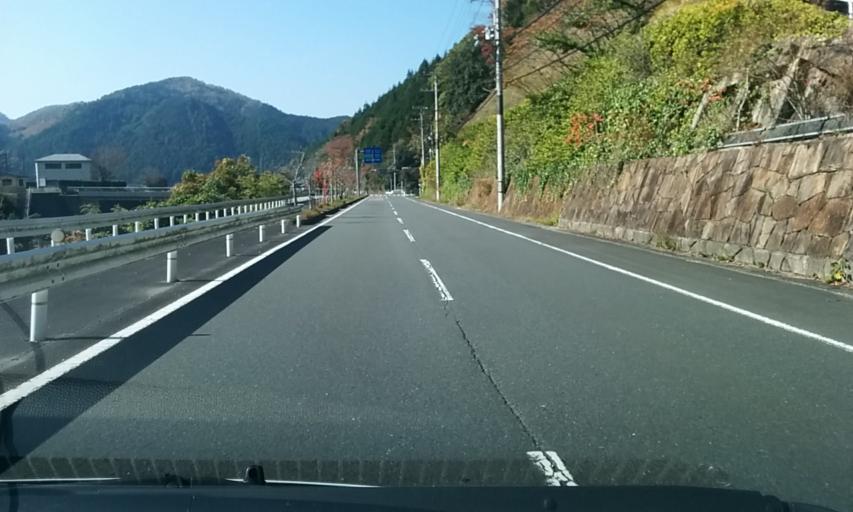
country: JP
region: Kyoto
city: Kameoka
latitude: 35.1542
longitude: 135.5153
